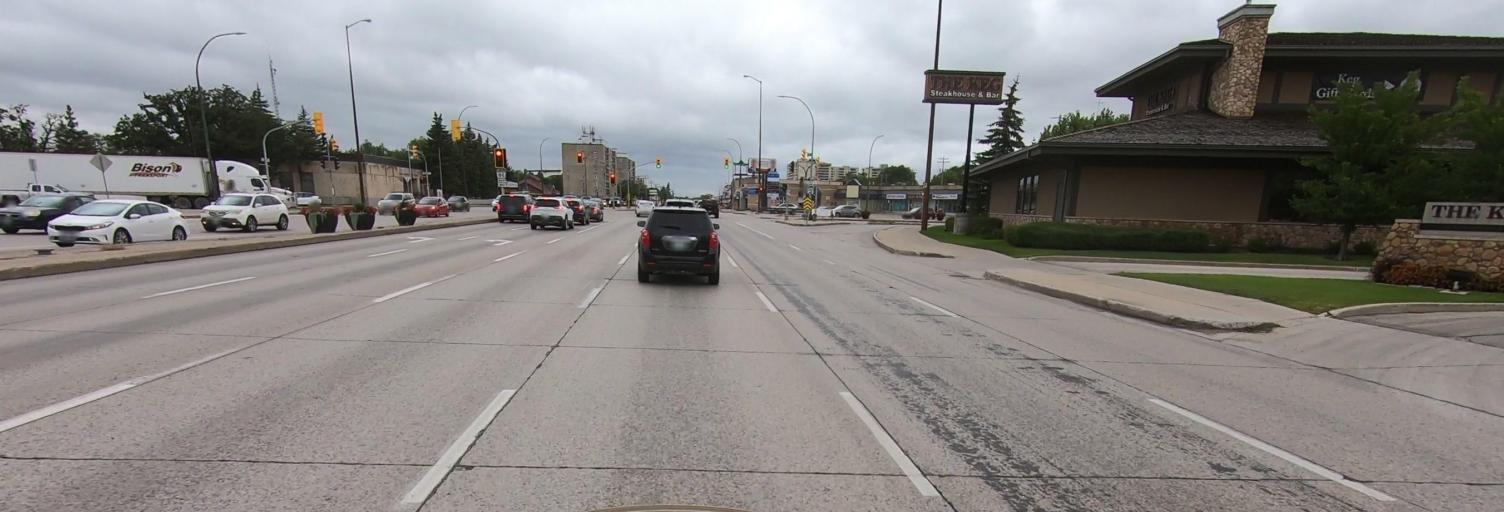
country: CA
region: Manitoba
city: Winnipeg
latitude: 49.8754
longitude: -97.2619
